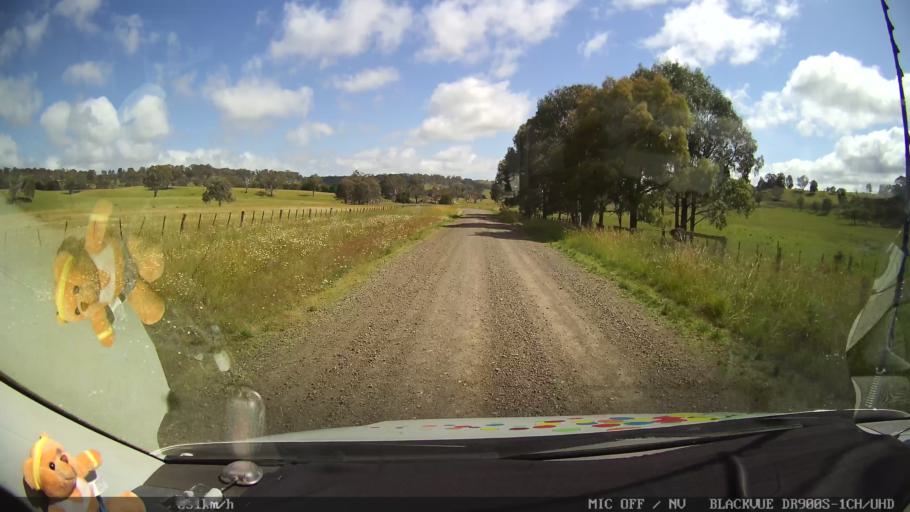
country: AU
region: New South Wales
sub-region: Glen Innes Severn
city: Glen Innes
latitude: -29.9701
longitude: 151.6996
